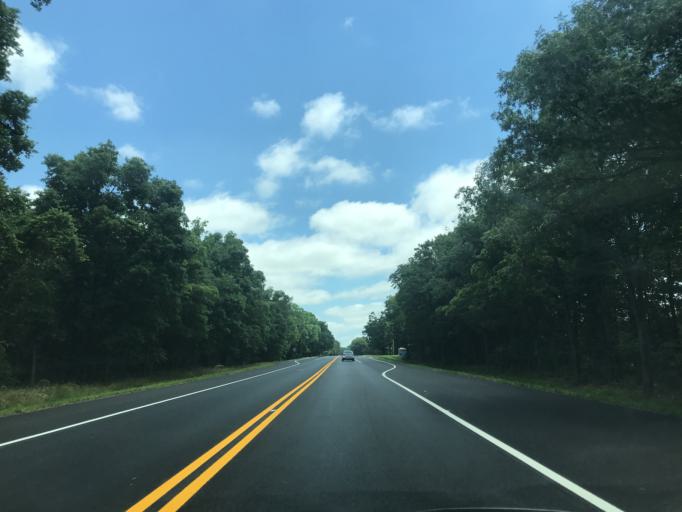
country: US
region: Maryland
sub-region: Caroline County
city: Federalsburg
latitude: 38.6904
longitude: -75.7596
